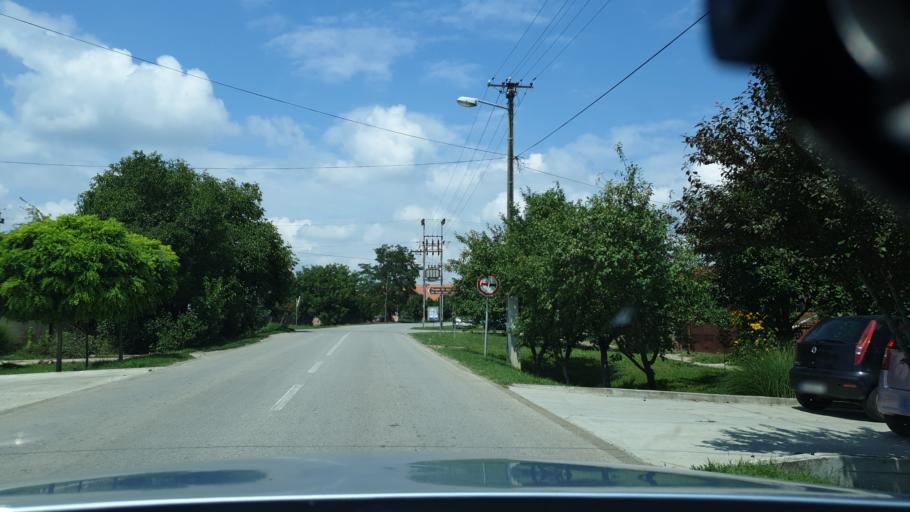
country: RS
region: Autonomna Pokrajina Vojvodina
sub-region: Juznobacki Okrug
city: Kovilj
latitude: 45.2382
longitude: 20.0277
